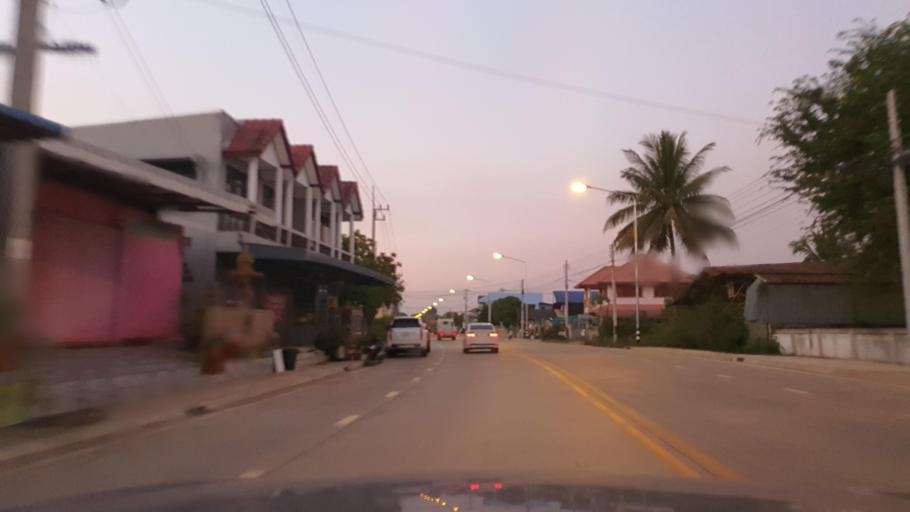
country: TH
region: Phayao
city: Dok Kham Tai
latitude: 19.1572
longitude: 99.9942
